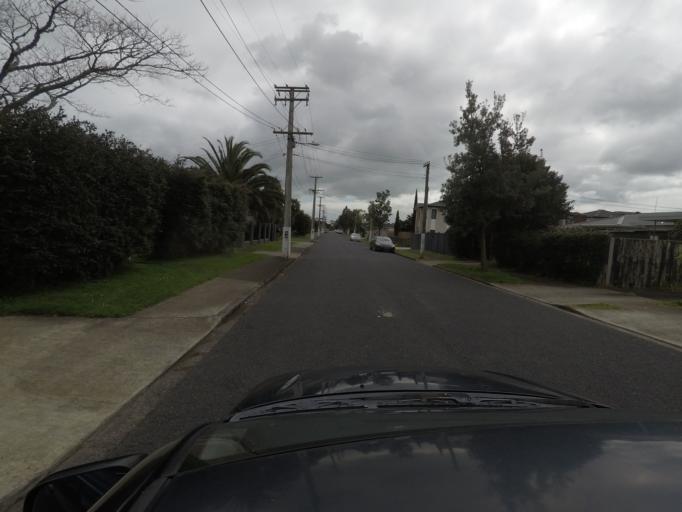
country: NZ
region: Auckland
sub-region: Auckland
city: Tamaki
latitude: -36.9354
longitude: 174.8546
